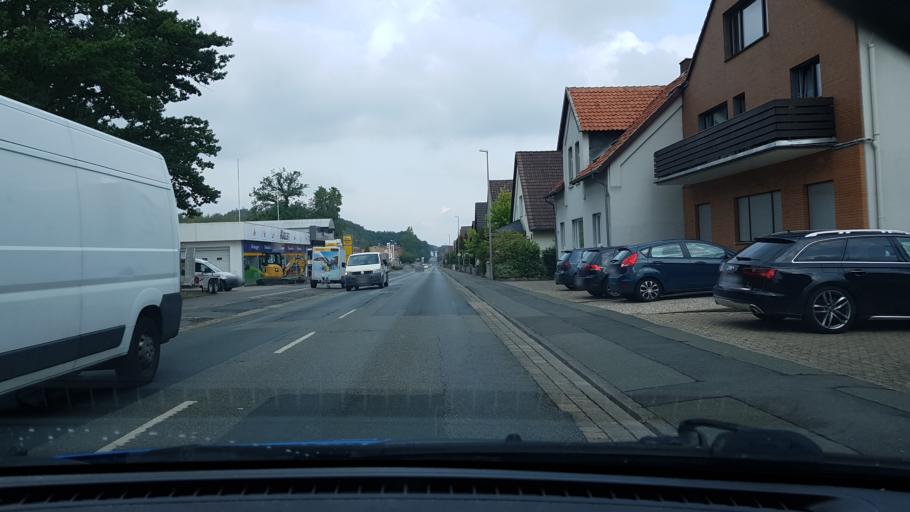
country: DE
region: Lower Saxony
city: Barsinghausen
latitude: 52.2939
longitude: 9.4819
